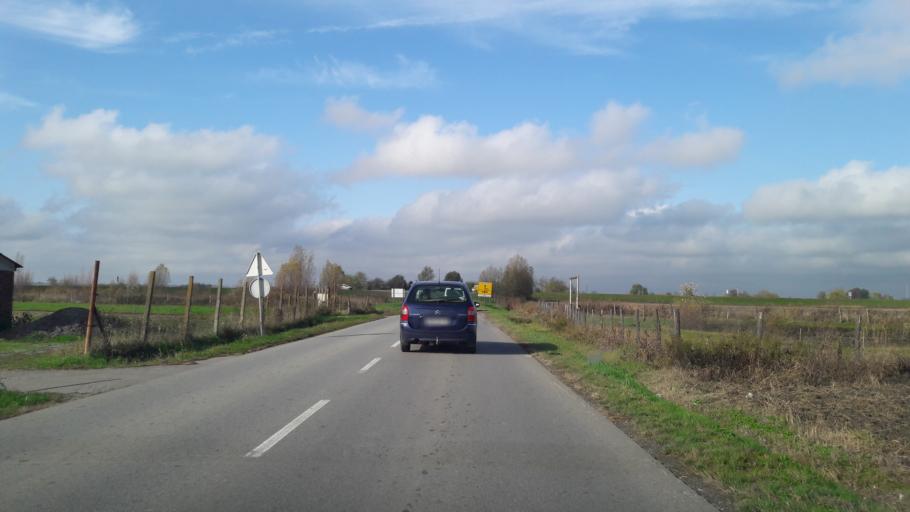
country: HR
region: Osjecko-Baranjska
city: Darda
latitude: 45.6196
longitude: 18.6791
